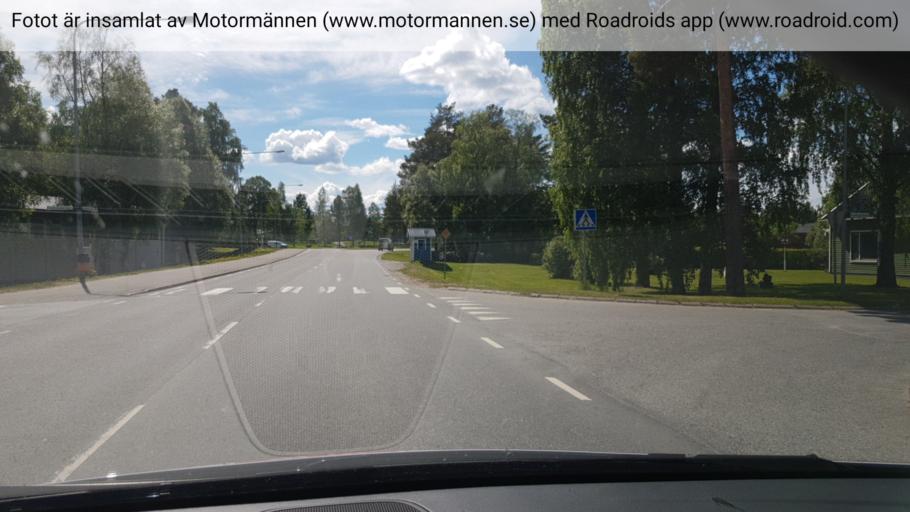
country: SE
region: Vaesterbotten
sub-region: Skelleftea Kommun
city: Burtraesk
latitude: 64.5127
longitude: 20.6486
